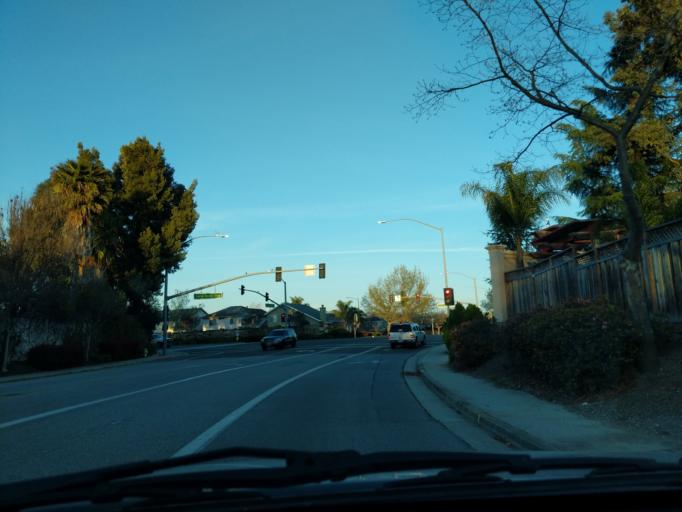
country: US
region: California
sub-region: Santa Clara County
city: Gilroy
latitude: 37.0279
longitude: -121.5989
